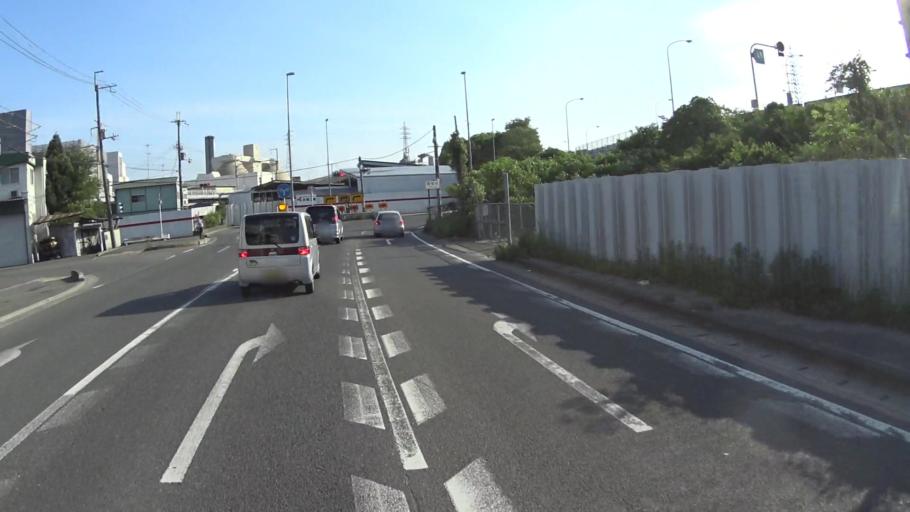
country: JP
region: Kyoto
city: Yawata
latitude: 34.9069
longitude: 135.7078
